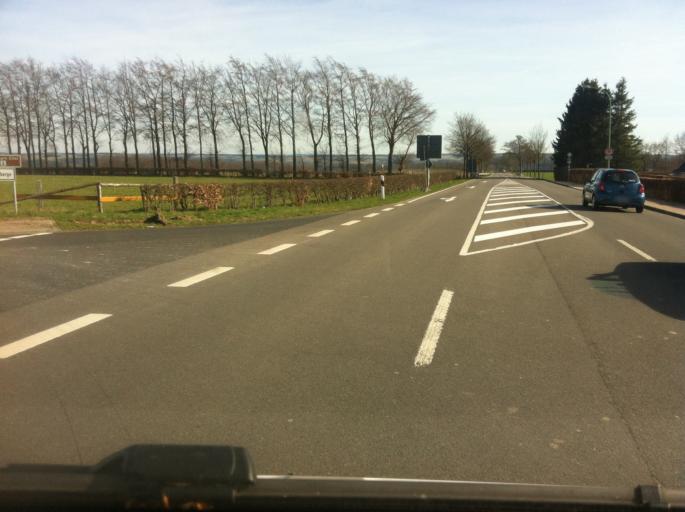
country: DE
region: North Rhine-Westphalia
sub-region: Regierungsbezirk Koln
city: Simmerath
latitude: 50.6029
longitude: 6.3399
